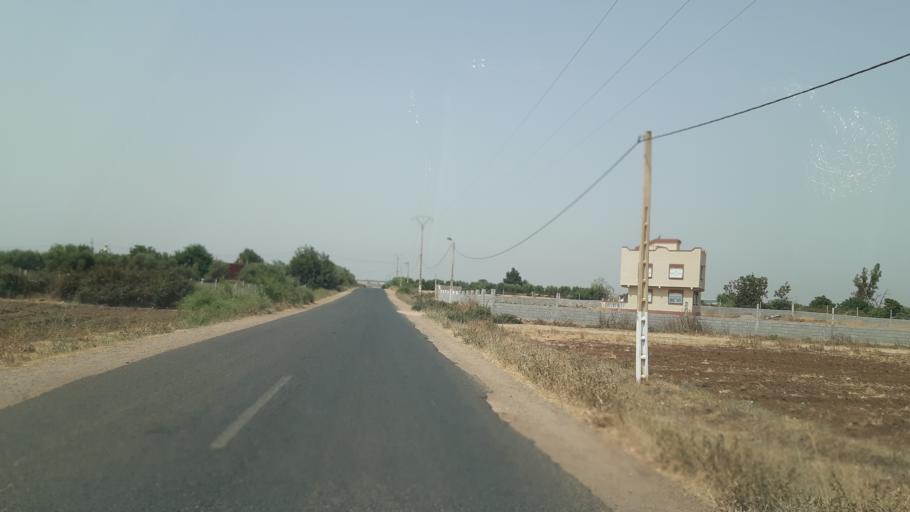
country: MA
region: Fes-Boulemane
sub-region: Fes
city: Oulad Tayeb
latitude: 33.8242
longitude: -5.1663
